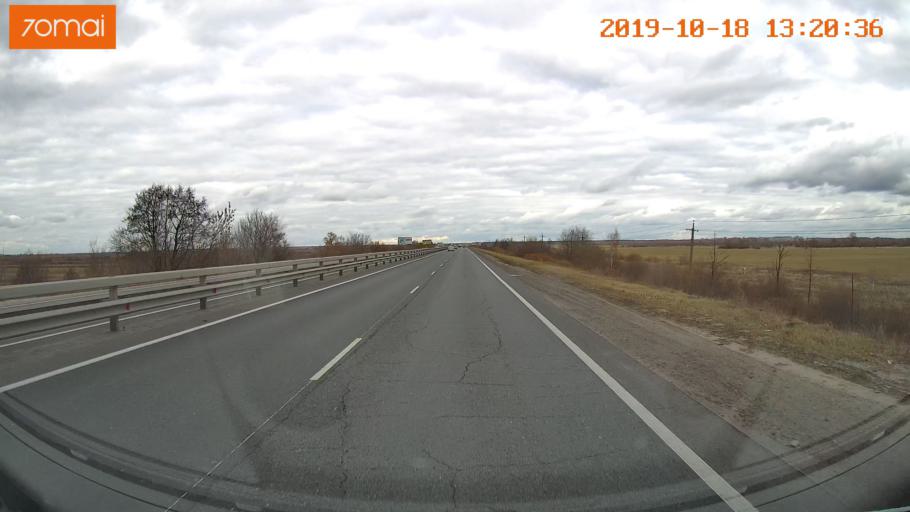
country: RU
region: Rjazan
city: Polyany
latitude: 54.6831
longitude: 39.8331
